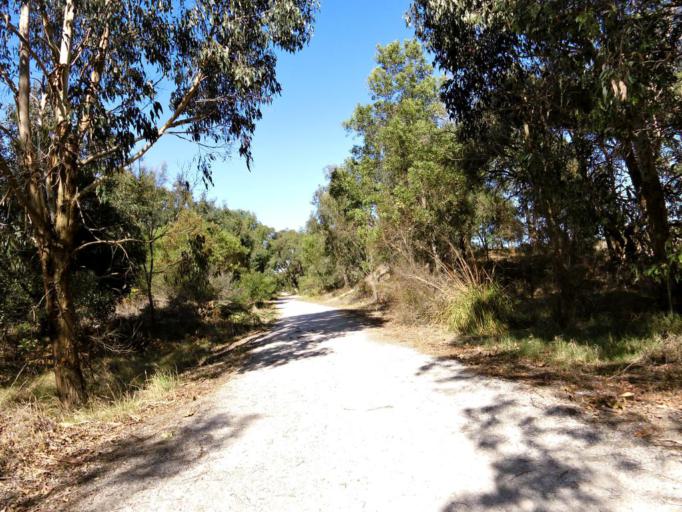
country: AU
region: Victoria
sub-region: Bass Coast
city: North Wonthaggi
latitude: -38.6102
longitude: 145.6021
